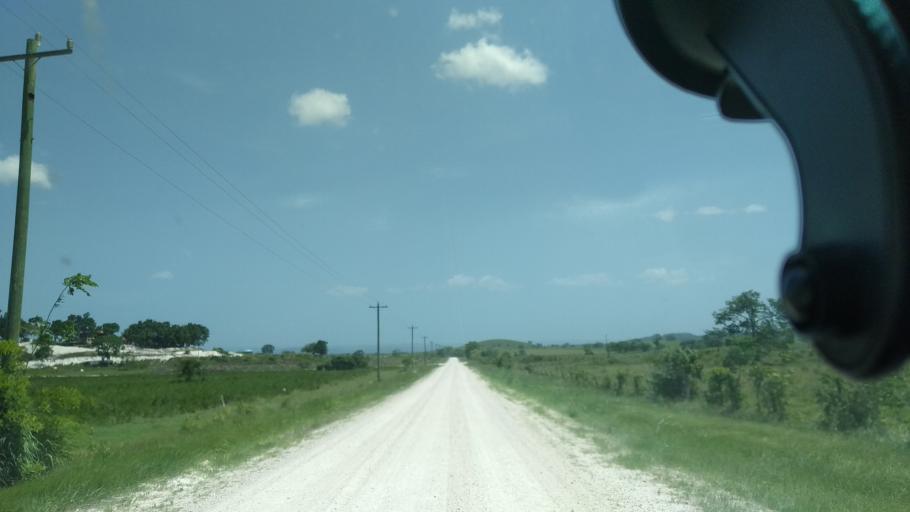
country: BZ
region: Cayo
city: San Ignacio
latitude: 17.3028
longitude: -89.0480
